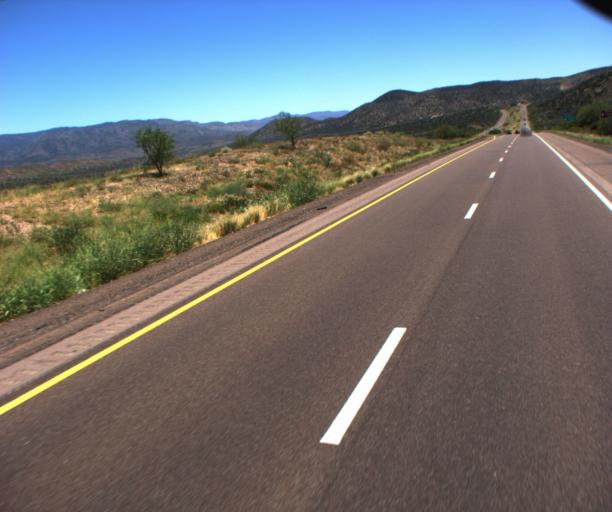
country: US
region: Arizona
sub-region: Gila County
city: Payson
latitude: 34.0389
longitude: -111.3694
